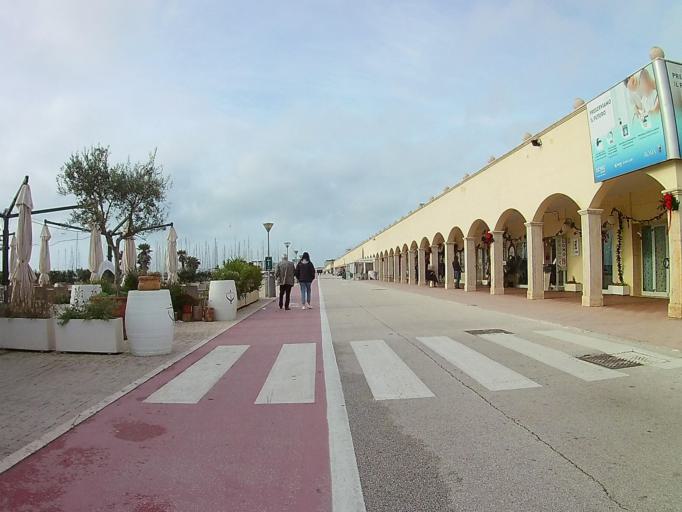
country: IT
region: Latium
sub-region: Citta metropolitana di Roma Capitale
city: Lido di Ostia
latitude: 41.7383
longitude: 12.2478
